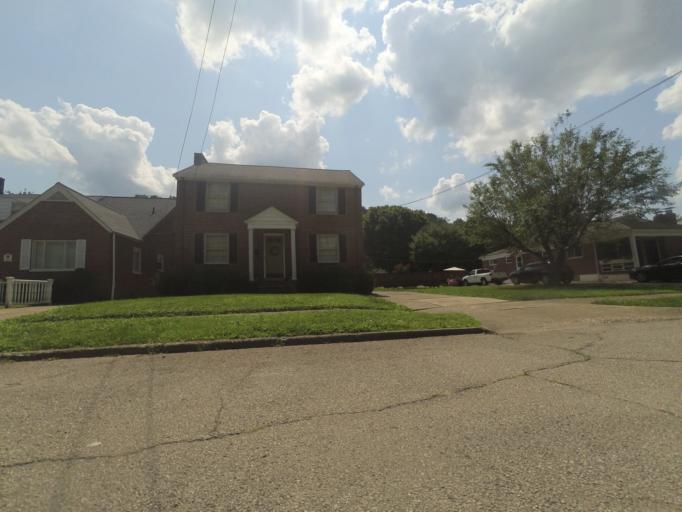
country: US
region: West Virginia
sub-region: Cabell County
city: Huntington
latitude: 38.4029
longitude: -82.4278
